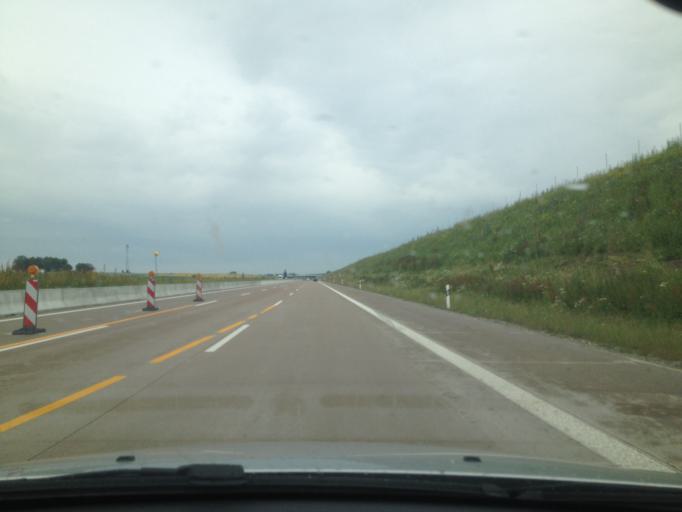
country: DE
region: Bavaria
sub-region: Swabia
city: Burgau
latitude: 48.4182
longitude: 10.3993
